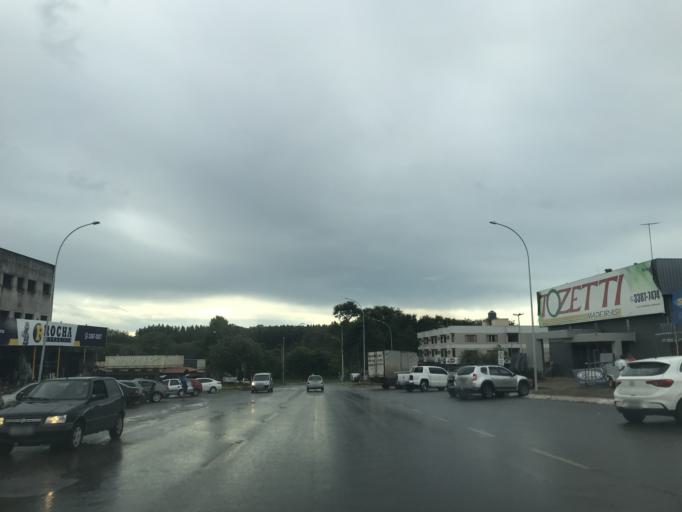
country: BR
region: Federal District
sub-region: Brasilia
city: Brasilia
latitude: -15.6419
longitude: -47.8082
